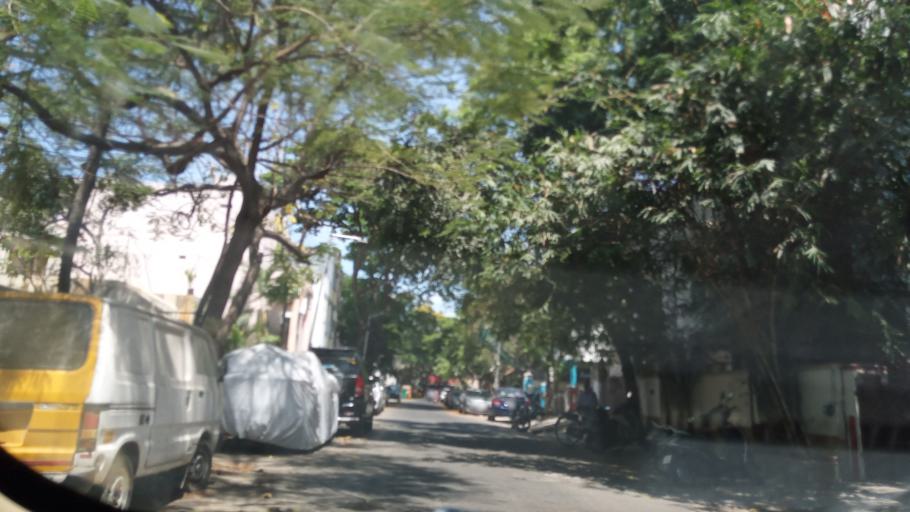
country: IN
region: Tamil Nadu
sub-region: Chennai
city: Chetput
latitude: 13.0389
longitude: 80.2222
